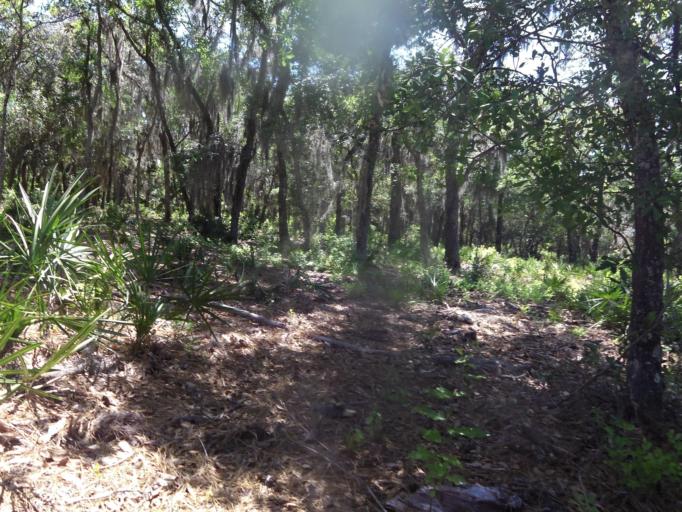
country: US
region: Florida
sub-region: Duval County
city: Atlantic Beach
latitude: 30.4453
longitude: -81.4760
